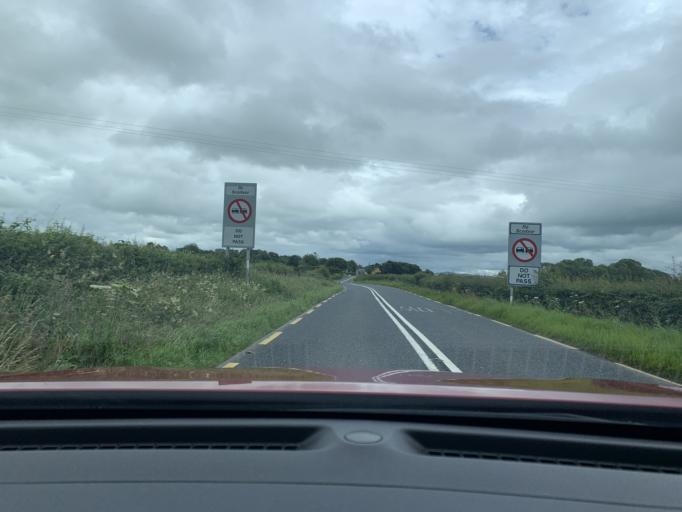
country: IE
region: Ulster
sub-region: County Donegal
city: Convoy
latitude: 54.8007
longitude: -7.6496
